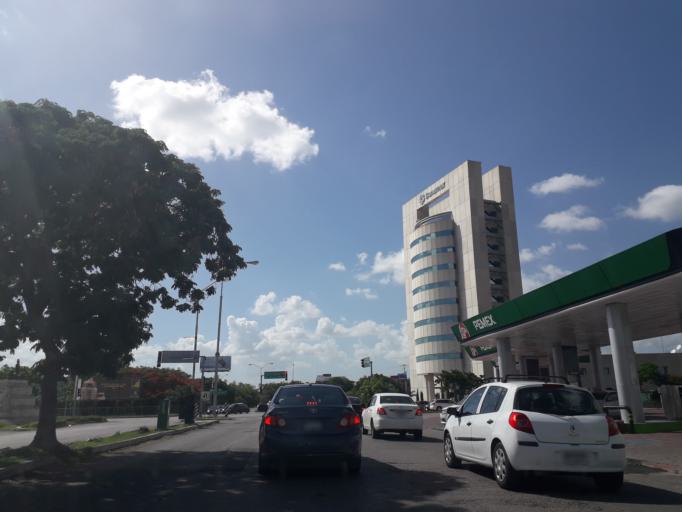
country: MX
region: Yucatan
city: Merida
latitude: 21.0257
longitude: -89.6240
